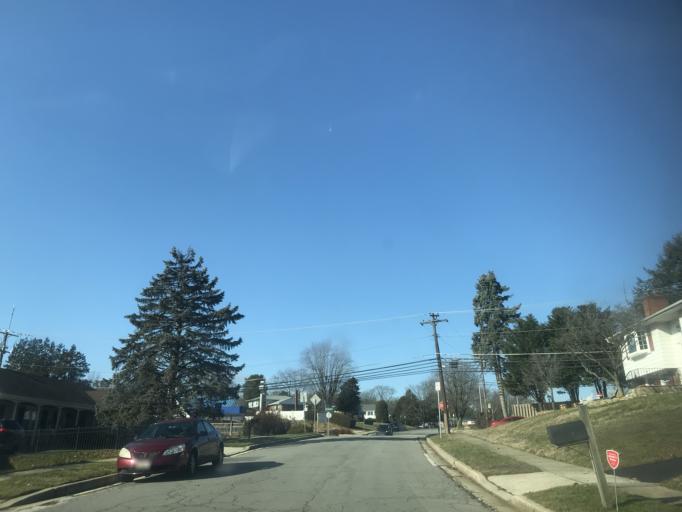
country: US
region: Maryland
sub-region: Baltimore County
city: Hampton
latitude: 39.4055
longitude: -76.5808
